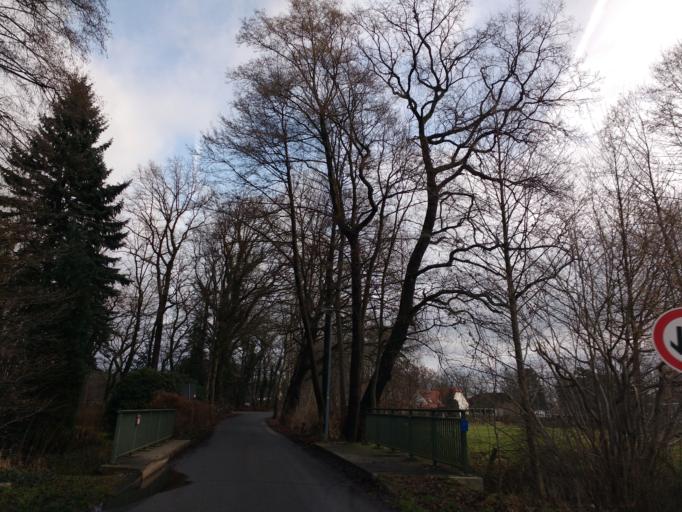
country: DE
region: North Rhine-Westphalia
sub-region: Regierungsbezirk Detmold
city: Hovelhof
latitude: 51.8293
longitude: 8.6815
